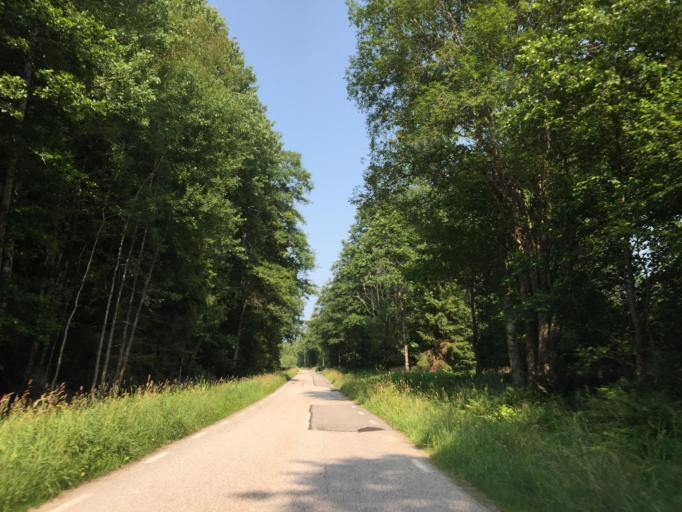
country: SE
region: Vaestra Goetaland
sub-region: Trollhattan
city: Sjuntorp
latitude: 58.2884
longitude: 12.1297
